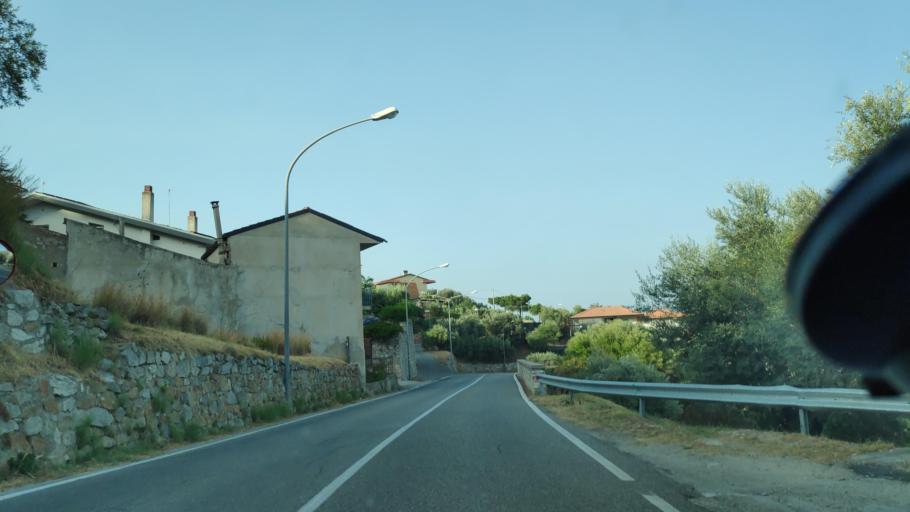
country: IT
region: Calabria
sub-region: Provincia di Catanzaro
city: Sant'Andrea Ionio Marina
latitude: 38.6194
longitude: 16.5430
